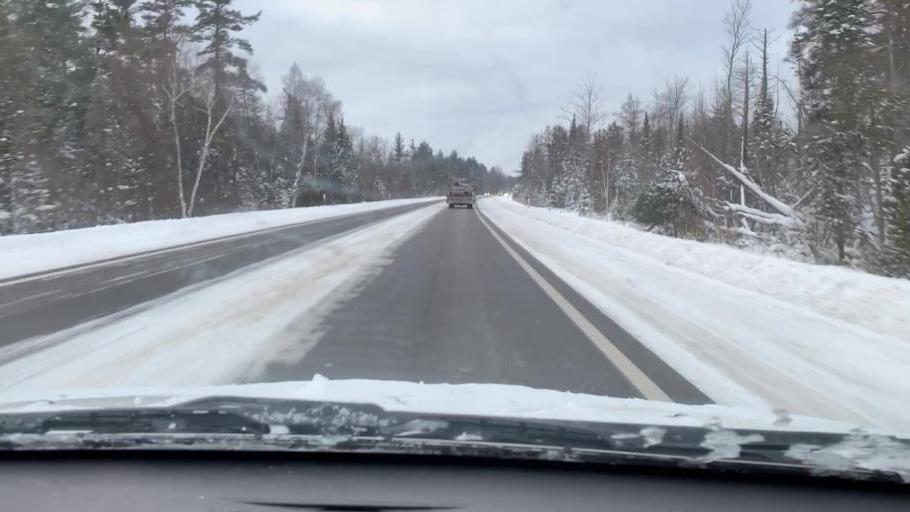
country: US
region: Michigan
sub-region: Kalkaska County
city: Kalkaska
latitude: 44.7023
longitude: -85.2021
